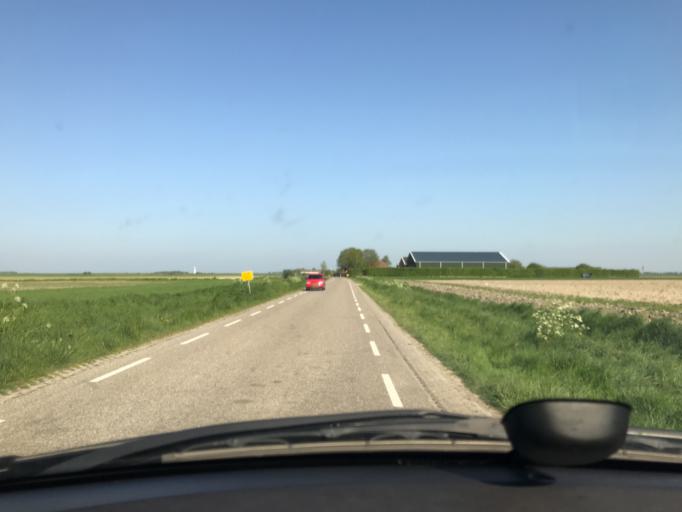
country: NL
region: Zeeland
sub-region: Gemeente Goes
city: Goes
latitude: 51.5399
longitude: 3.8167
